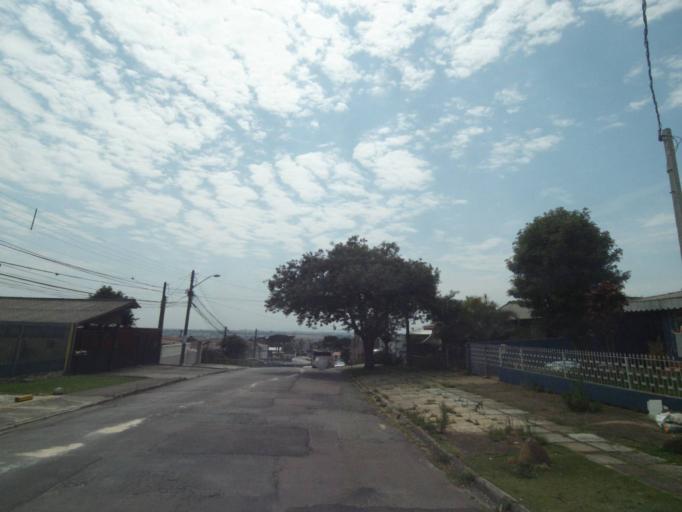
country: BR
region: Parana
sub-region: Pinhais
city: Pinhais
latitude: -25.3959
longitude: -49.2098
